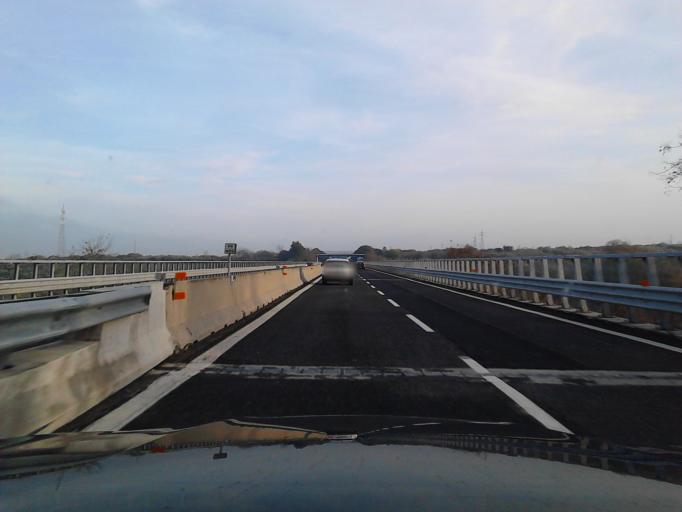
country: IT
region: Abruzzo
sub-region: Provincia di Chieti
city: Ortona
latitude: 42.3346
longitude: 14.3698
